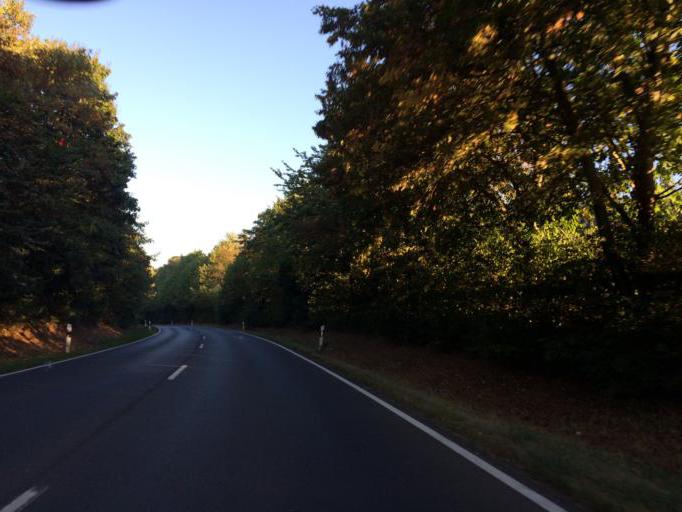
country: DE
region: North Rhine-Westphalia
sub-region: Regierungsbezirk Koln
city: Wachtberg
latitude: 50.6400
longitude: 7.1083
